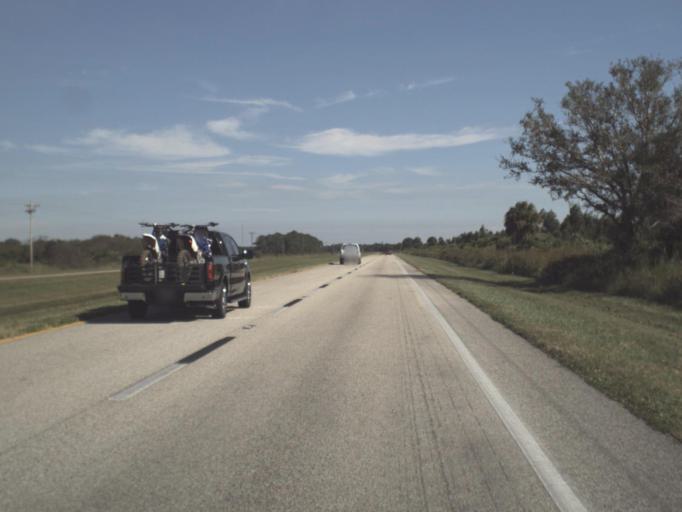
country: US
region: Florida
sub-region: Glades County
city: Moore Haven
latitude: 26.9072
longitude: -81.2658
